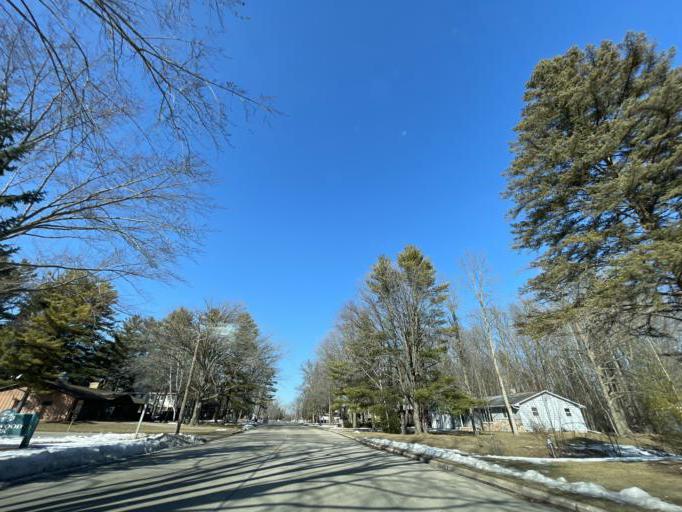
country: US
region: Wisconsin
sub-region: Brown County
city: Howard
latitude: 44.5690
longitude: -88.0803
